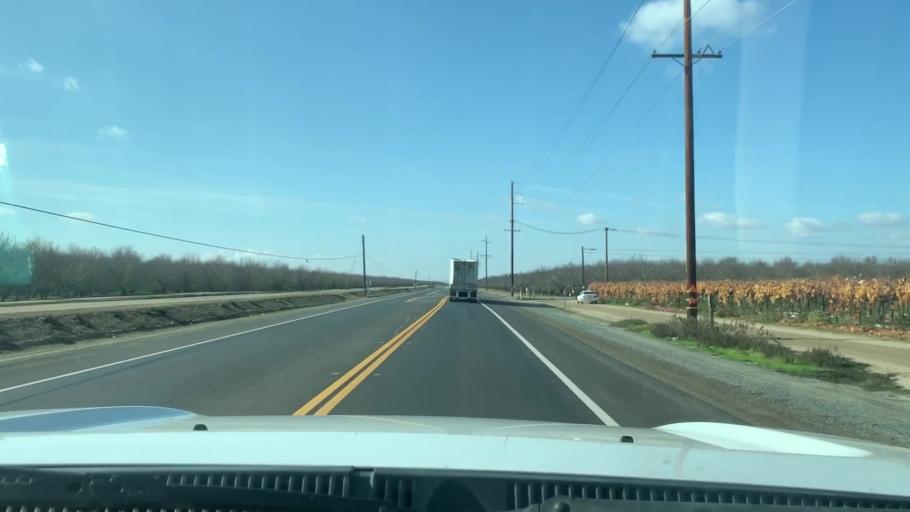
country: US
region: California
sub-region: Kern County
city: Wasco
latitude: 35.6018
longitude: -119.2757
